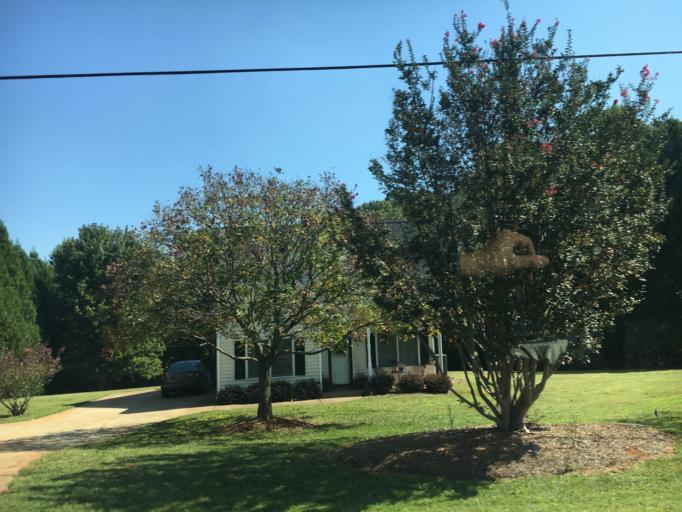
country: US
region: South Carolina
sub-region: Spartanburg County
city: Duncan
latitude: 34.8869
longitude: -82.1113
